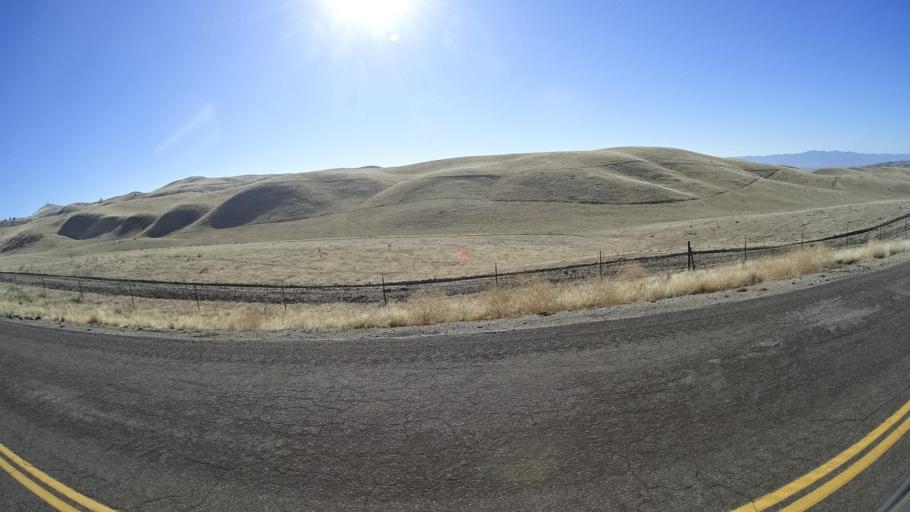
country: US
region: California
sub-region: Kern County
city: Maricopa
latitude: 34.9496
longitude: -119.4212
